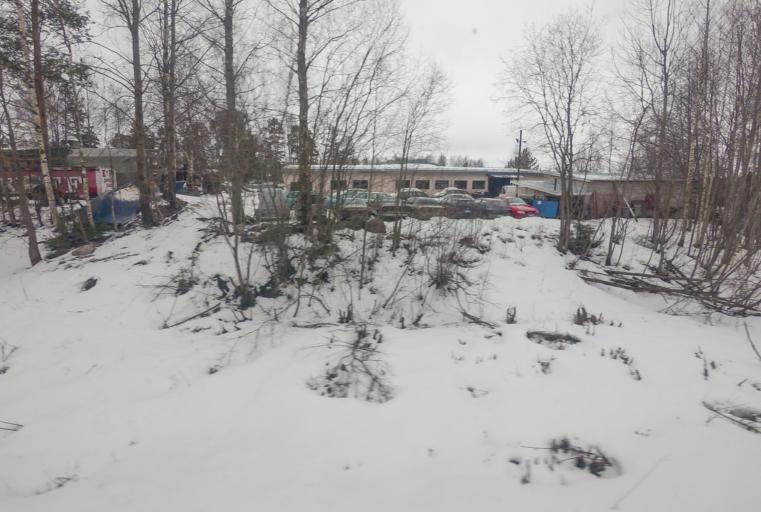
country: FI
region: Southern Savonia
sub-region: Savonlinna
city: Savonlinna
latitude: 61.8591
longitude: 28.9466
